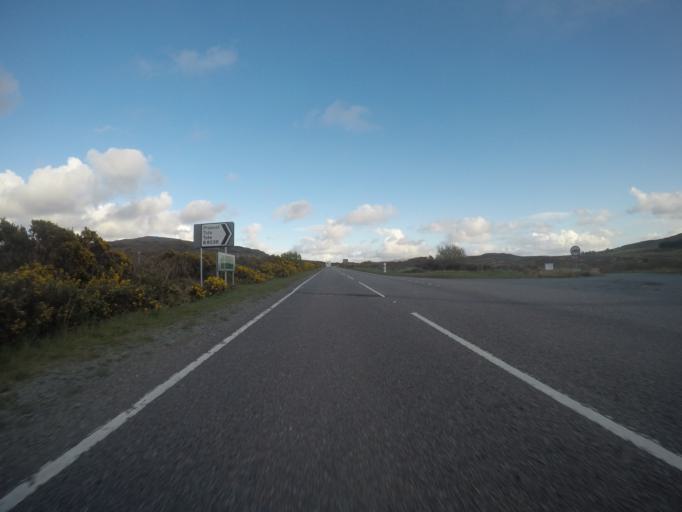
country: GB
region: Scotland
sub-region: Highland
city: Portree
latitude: 57.4739
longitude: -6.2978
